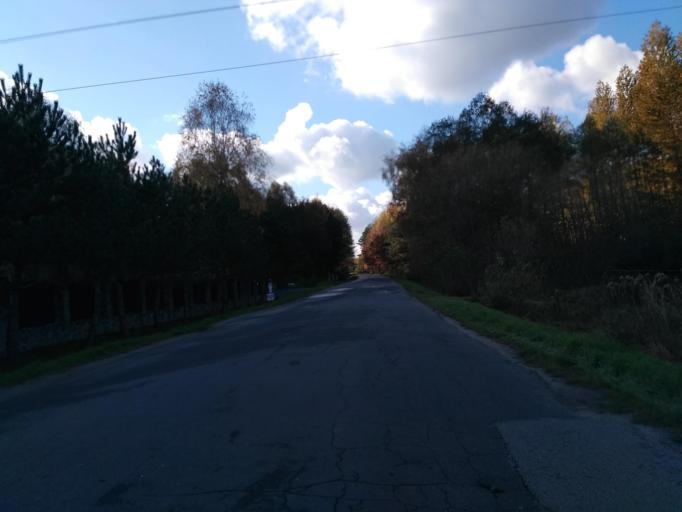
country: PL
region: Subcarpathian Voivodeship
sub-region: Powiat rzeszowski
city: Glogow Malopolski
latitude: 50.1434
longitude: 21.9464
